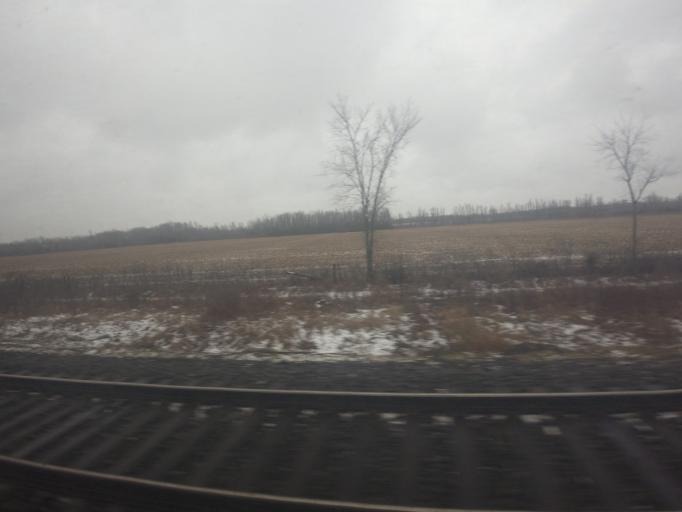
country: CA
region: Ontario
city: Deseronto
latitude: 44.2153
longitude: -77.1742
